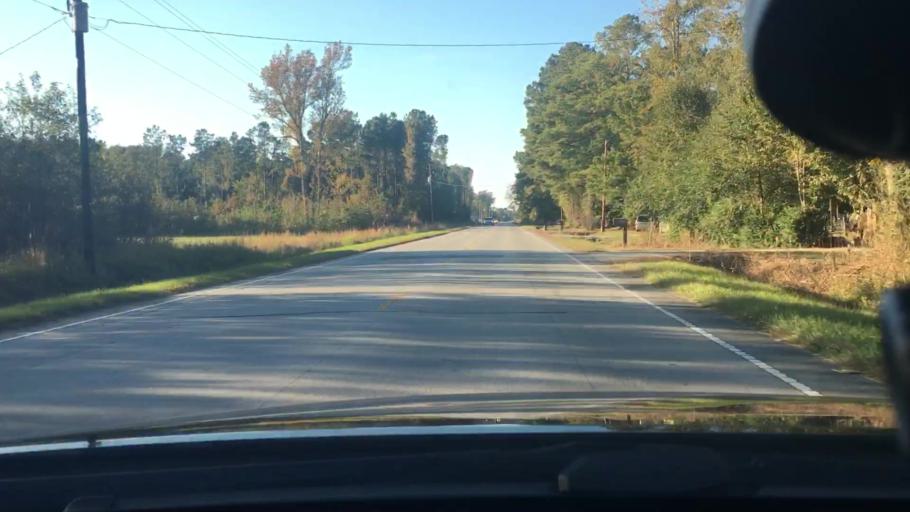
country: US
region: North Carolina
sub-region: Craven County
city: Vanceboro
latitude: 35.3456
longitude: -77.1825
